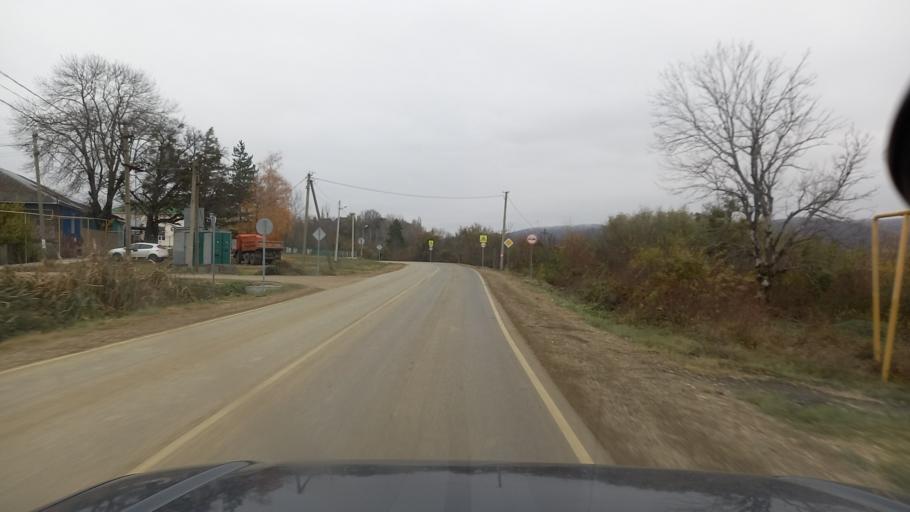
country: RU
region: Krasnodarskiy
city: Goryachiy Klyuch
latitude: 44.5168
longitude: 39.2942
